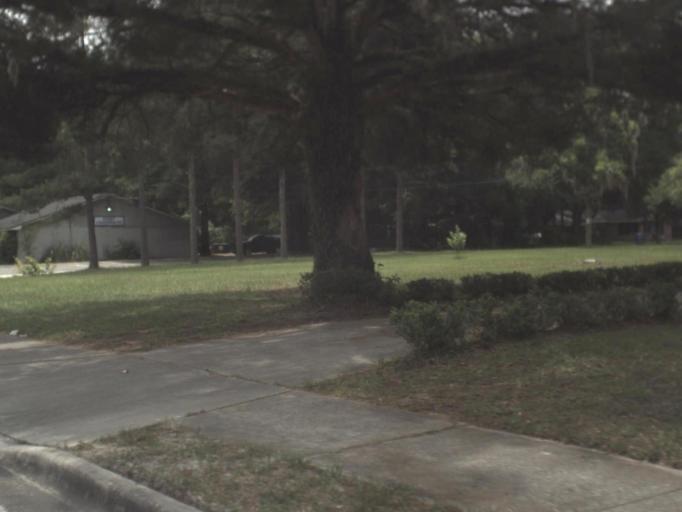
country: US
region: Florida
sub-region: Duval County
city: Jacksonville
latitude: 30.4388
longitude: -81.6902
